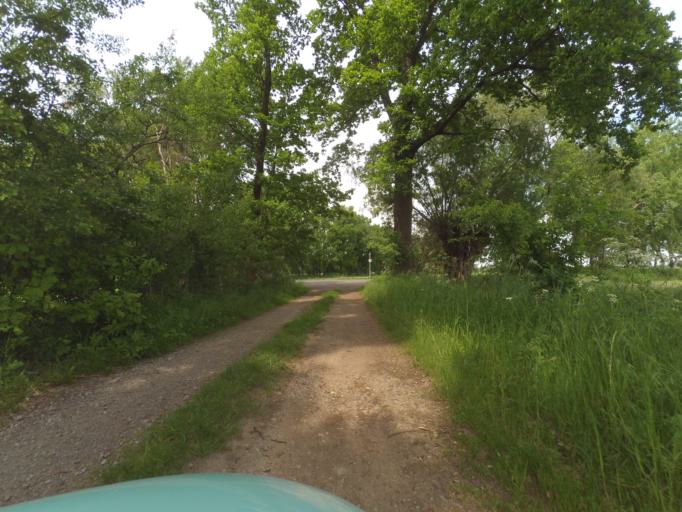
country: DE
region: Lower Saxony
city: Arpke
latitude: 52.3532
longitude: 10.1374
